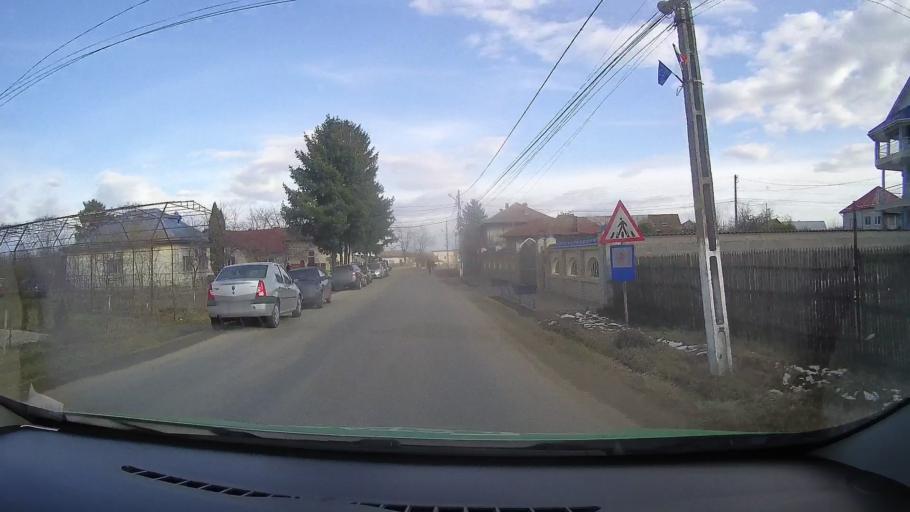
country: RO
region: Dambovita
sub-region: Comuna Comisani
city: Lazuri
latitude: 44.8689
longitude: 25.5253
